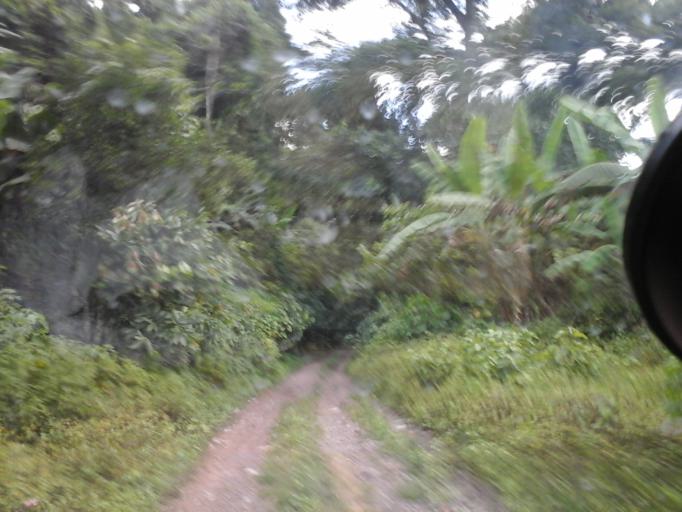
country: CO
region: Cesar
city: Manaure Balcon del Cesar
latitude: 10.2940
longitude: -73.0755
